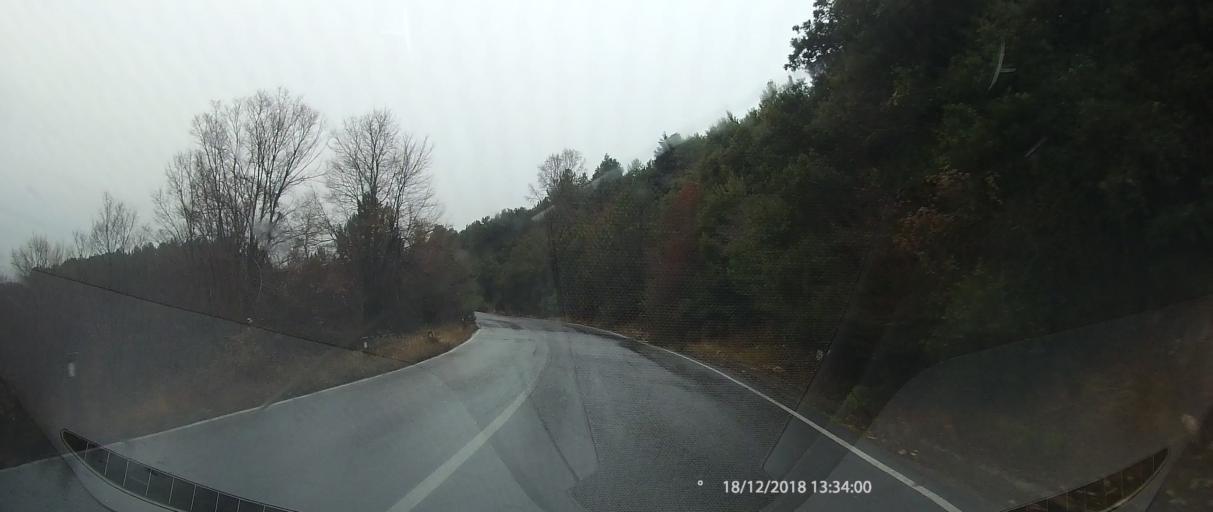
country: GR
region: Central Macedonia
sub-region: Nomos Pierias
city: Litochoro
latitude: 40.1151
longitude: 22.4830
